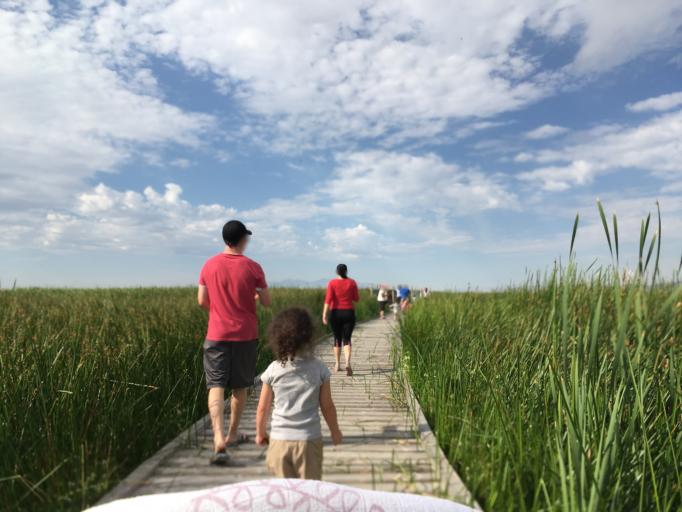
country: US
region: Utah
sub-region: Davis County
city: Layton
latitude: 41.0376
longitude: -112.0238
